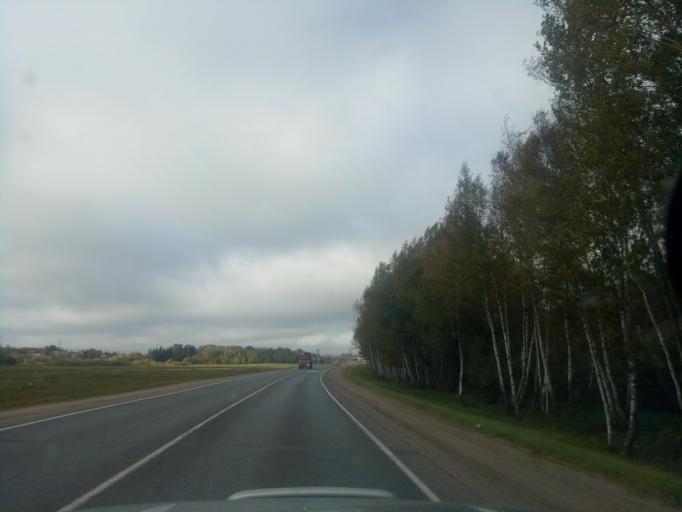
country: BY
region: Minsk
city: Zaslawye
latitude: 53.9939
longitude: 27.2945
